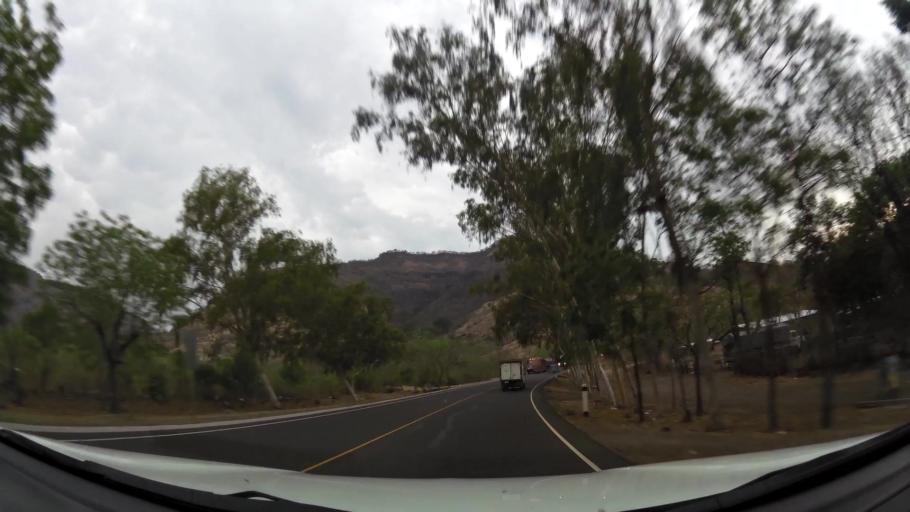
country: NI
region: Leon
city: Santa Rosa del Penon
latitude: 12.9365
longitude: -86.2163
